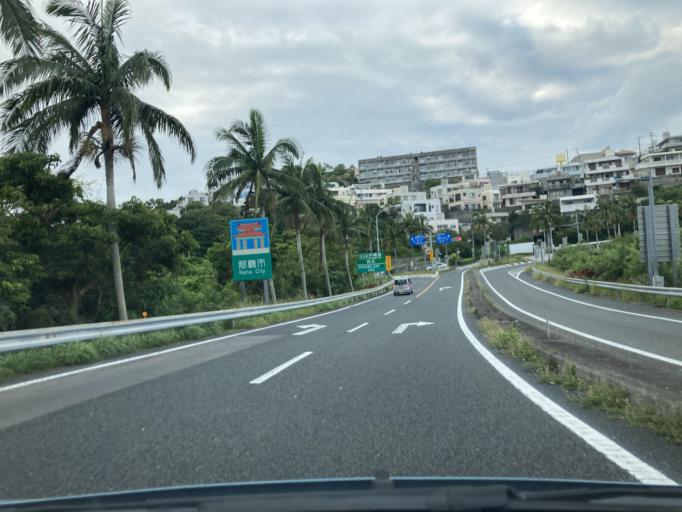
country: JP
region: Okinawa
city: Naha-shi
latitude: 26.2116
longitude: 127.7249
